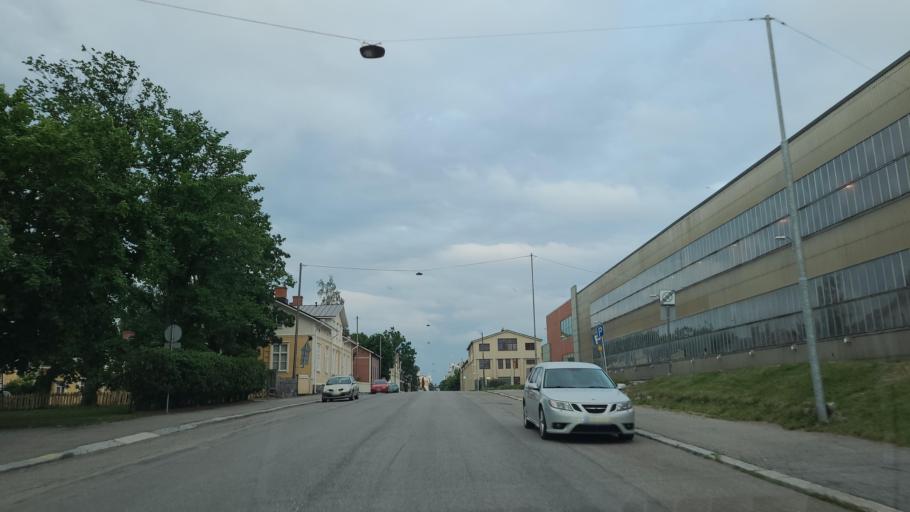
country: FI
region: Ostrobothnia
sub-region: Vaasa
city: Vaasa
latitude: 63.1039
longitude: 21.6121
